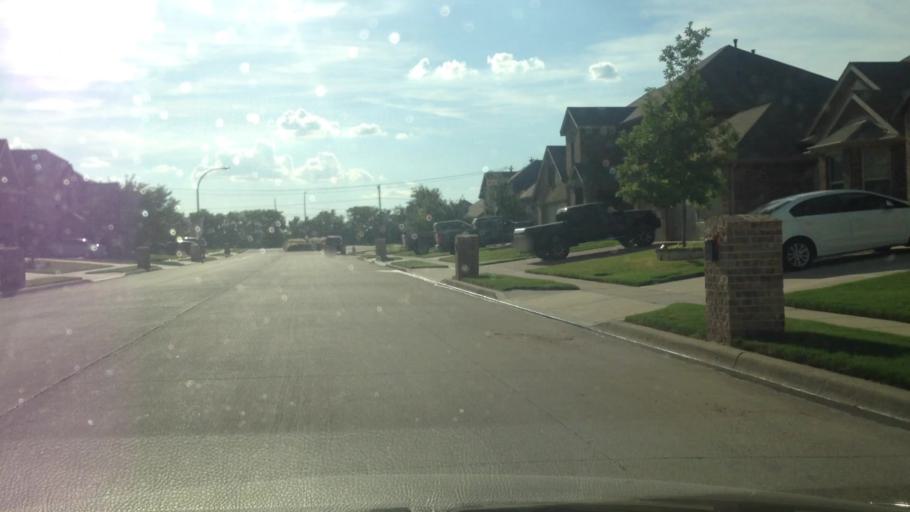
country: US
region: Texas
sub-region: Tarrant County
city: Haslet
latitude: 32.9375
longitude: -97.3904
